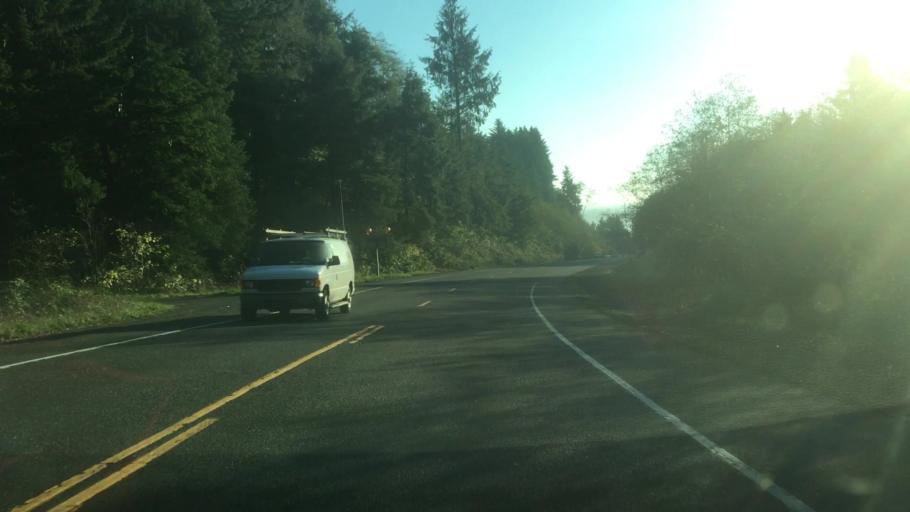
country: US
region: Oregon
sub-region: Clatsop County
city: Cannon Beach
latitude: 45.9104
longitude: -123.9495
